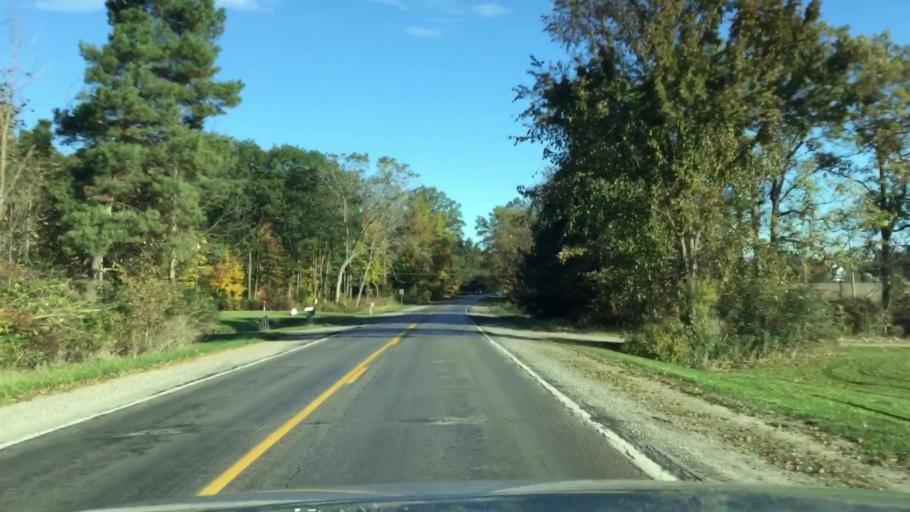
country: US
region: Michigan
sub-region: Shiawassee County
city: Durand
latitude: 42.9522
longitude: -83.9298
